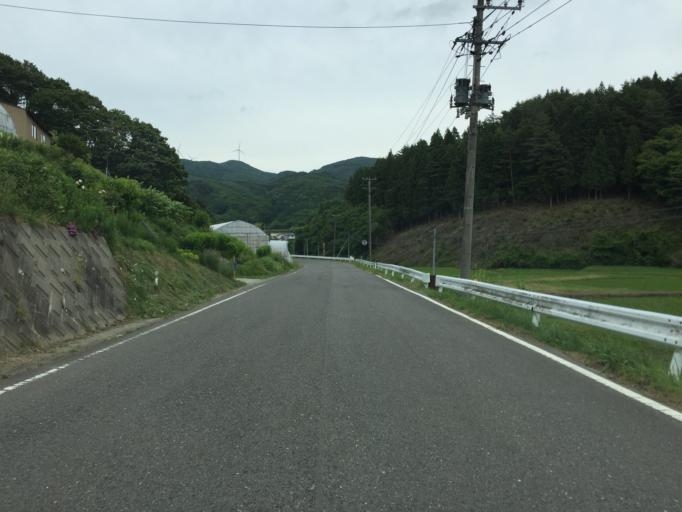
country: JP
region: Fukushima
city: Funehikimachi-funehiki
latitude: 37.3973
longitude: 140.6875
